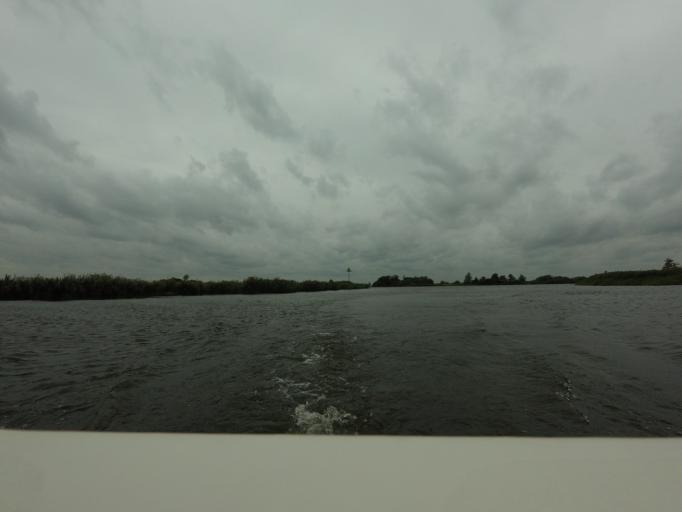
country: NL
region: Friesland
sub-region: Gemeente Boarnsterhim
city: Aldeboarn
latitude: 53.0977
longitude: 5.9013
